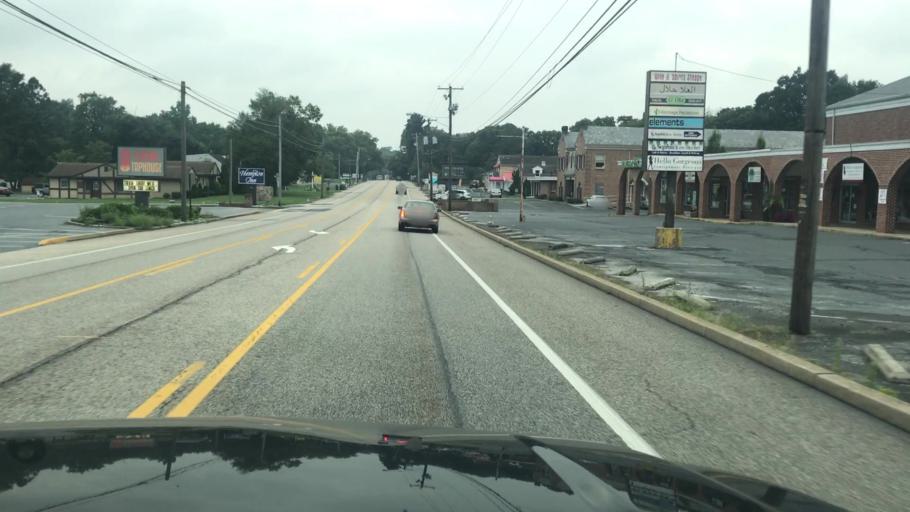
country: US
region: Pennsylvania
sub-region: Cumberland County
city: Shiremanstown
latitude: 40.2390
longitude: -76.9456
